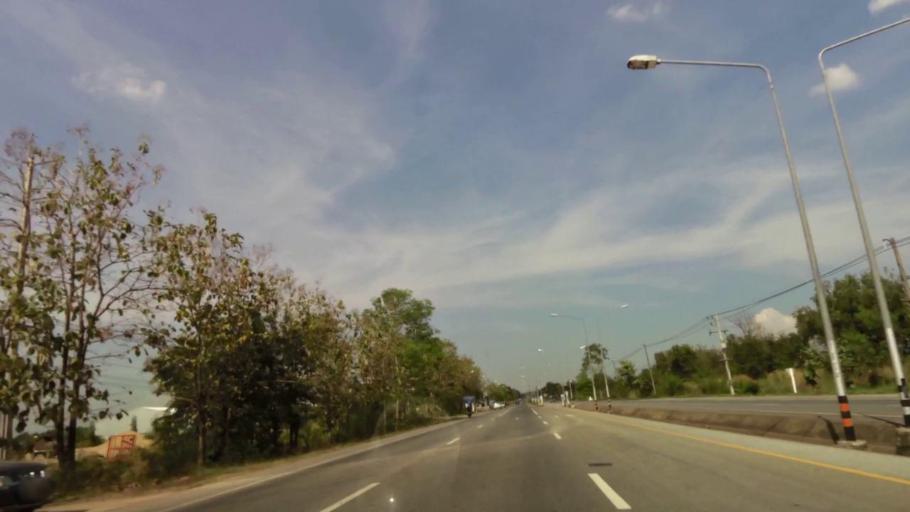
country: TH
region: Uttaradit
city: Tron
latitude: 17.5185
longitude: 100.2194
